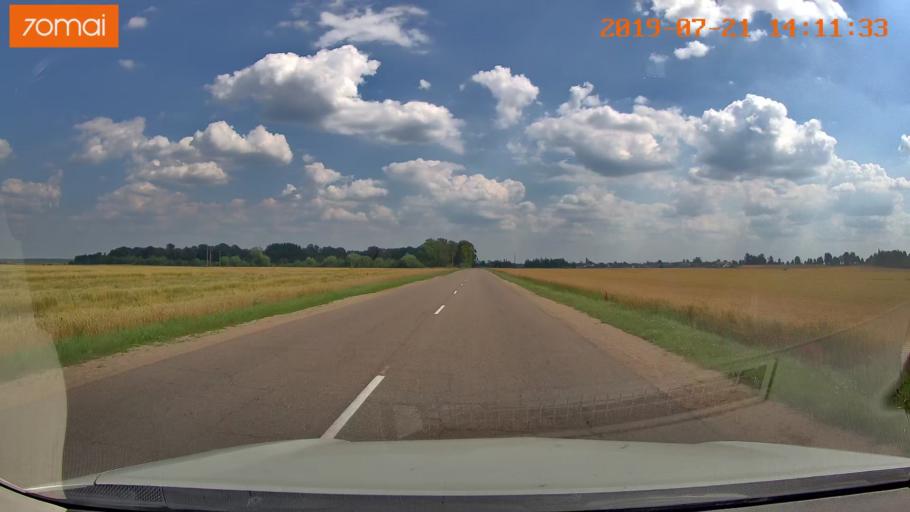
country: BY
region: Grodnenskaya
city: Karelichy
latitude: 53.6568
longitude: 26.1549
